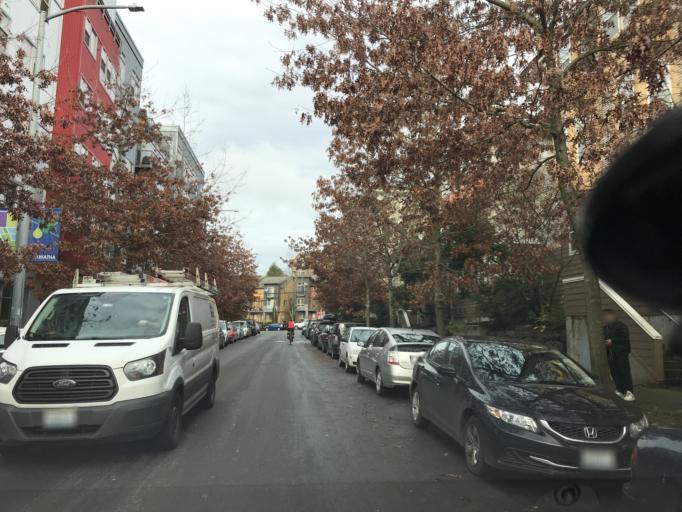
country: US
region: Washington
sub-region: King County
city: Seattle
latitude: 47.5951
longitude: -122.3096
